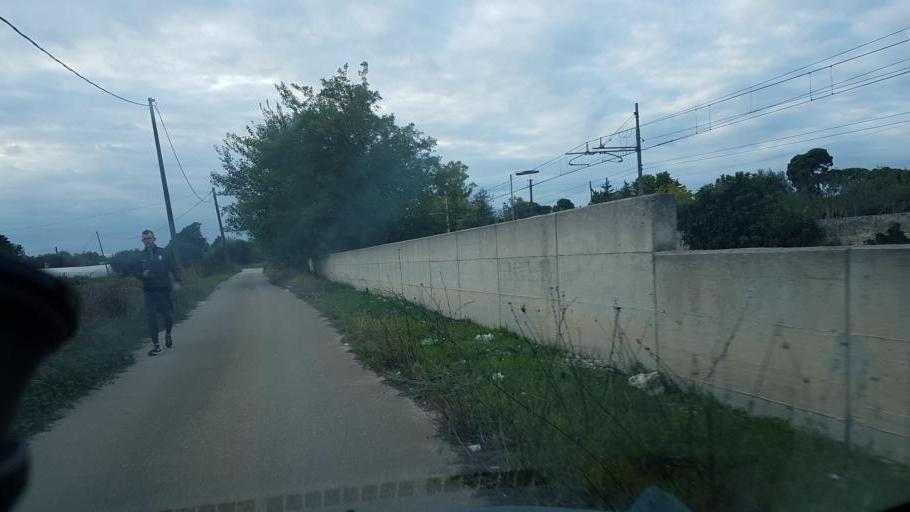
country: IT
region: Apulia
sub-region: Provincia di Brindisi
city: Oria
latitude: 40.5086
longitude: 17.6427
